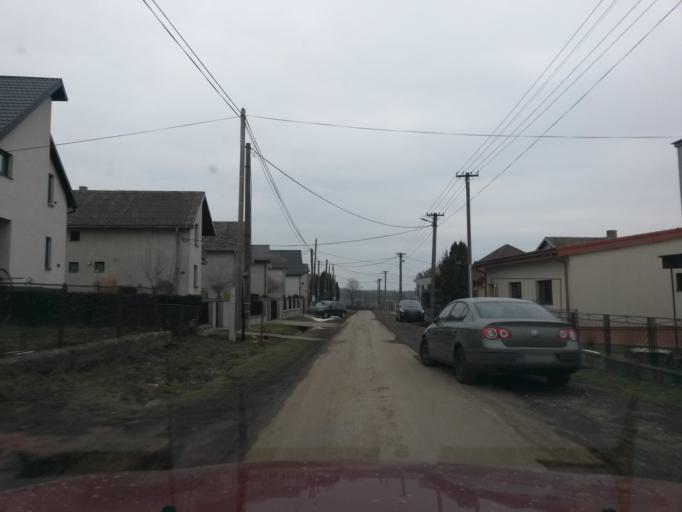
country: SK
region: Kosicky
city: Trebisov
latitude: 48.6793
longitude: 21.8133
